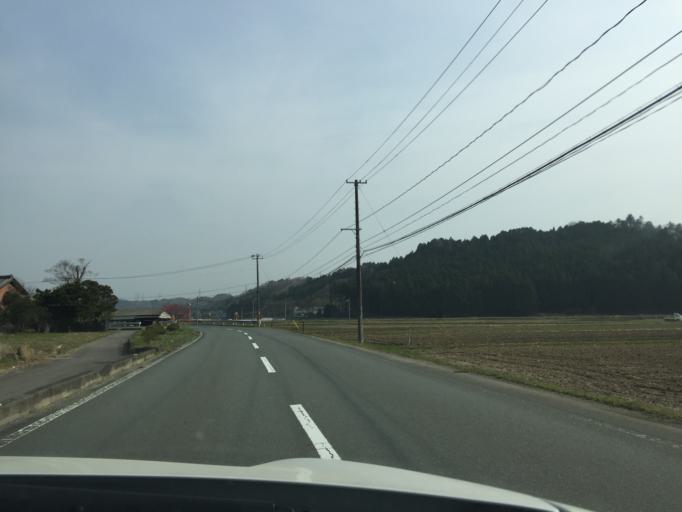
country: JP
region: Fukushima
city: Iwaki
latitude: 36.9708
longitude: 140.8026
